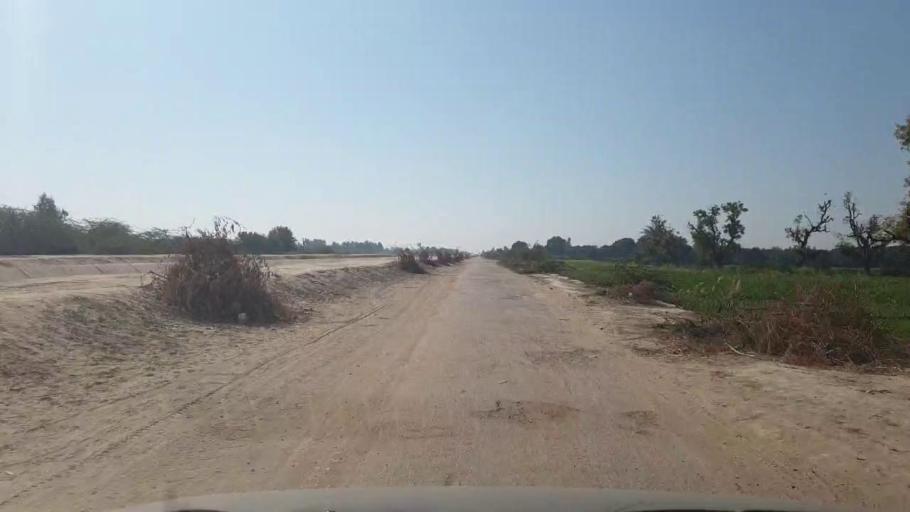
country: PK
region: Sindh
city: Mirwah Gorchani
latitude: 25.3045
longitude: 69.1028
